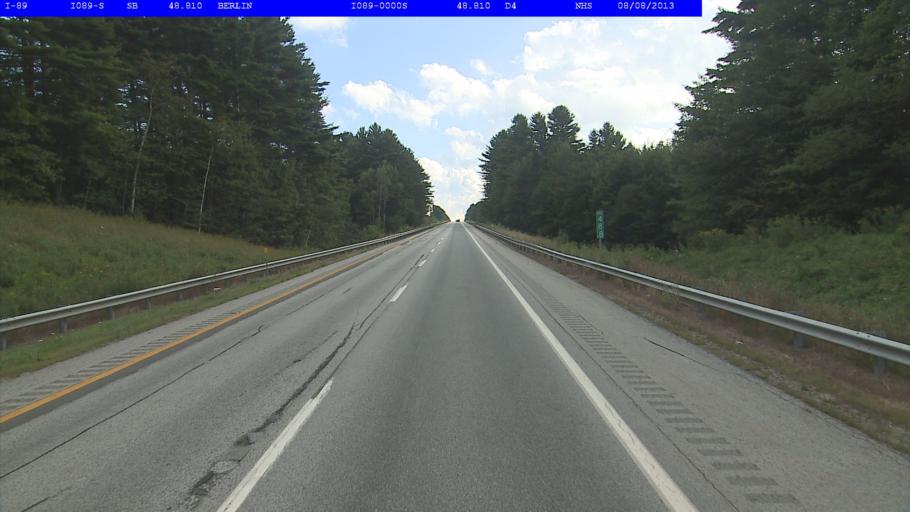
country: US
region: Vermont
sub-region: Washington County
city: Montpelier
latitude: 44.1951
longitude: -72.5774
